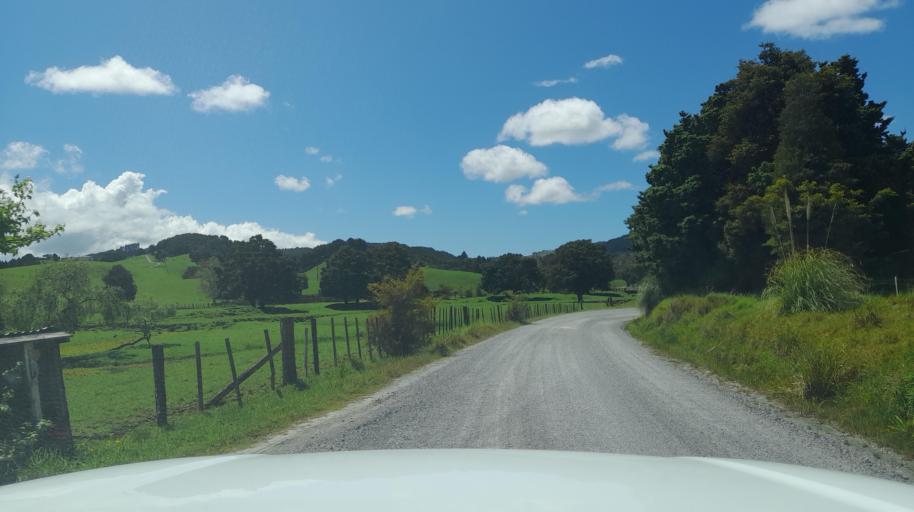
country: NZ
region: Northland
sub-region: Far North District
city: Kaitaia
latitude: -35.1174
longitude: 173.3937
